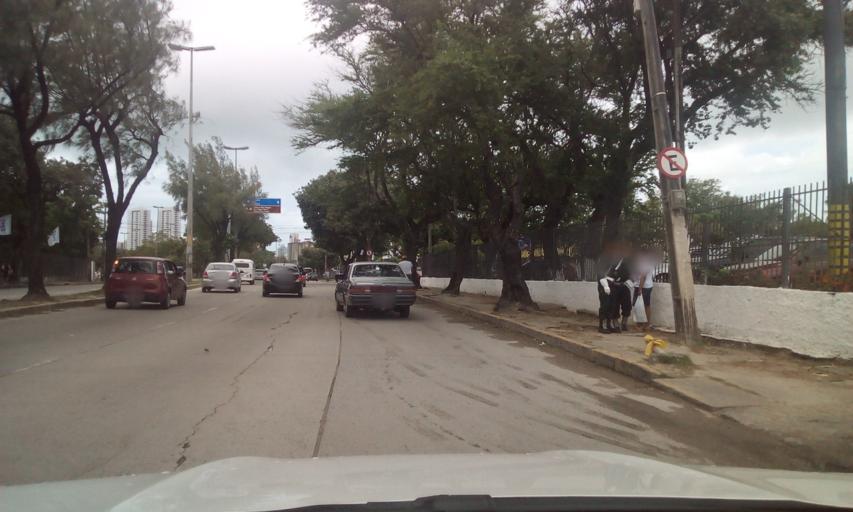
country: BR
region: Pernambuco
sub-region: Recife
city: Recife
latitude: -8.1216
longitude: -34.9184
